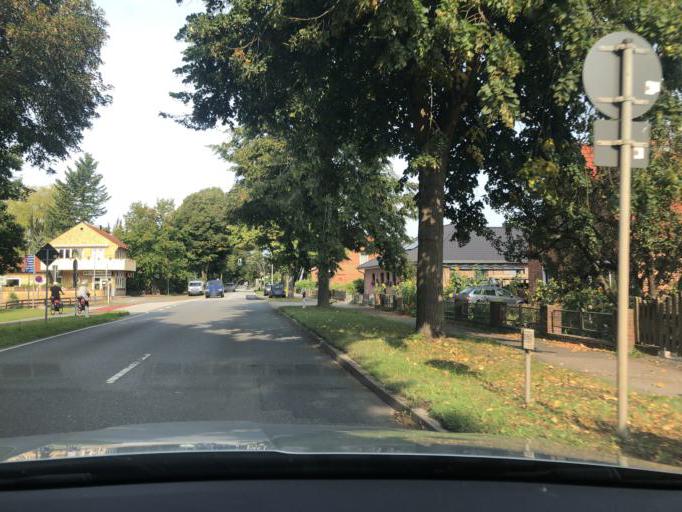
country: DE
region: Schleswig-Holstein
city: Gross Gronau
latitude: 53.8102
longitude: 10.7463
